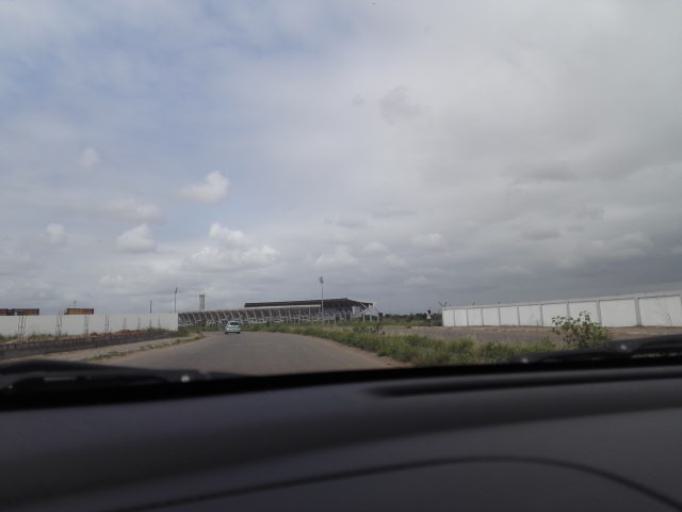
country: MZ
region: Maputo City
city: Maputo
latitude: -25.8237
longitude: 32.5817
